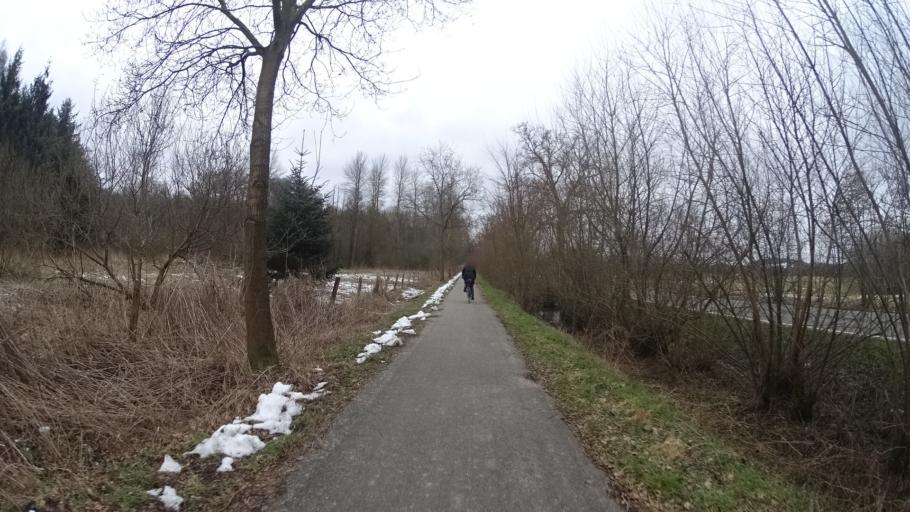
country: DE
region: Schleswig-Holstein
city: Malente
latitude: 54.1935
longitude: 10.5634
